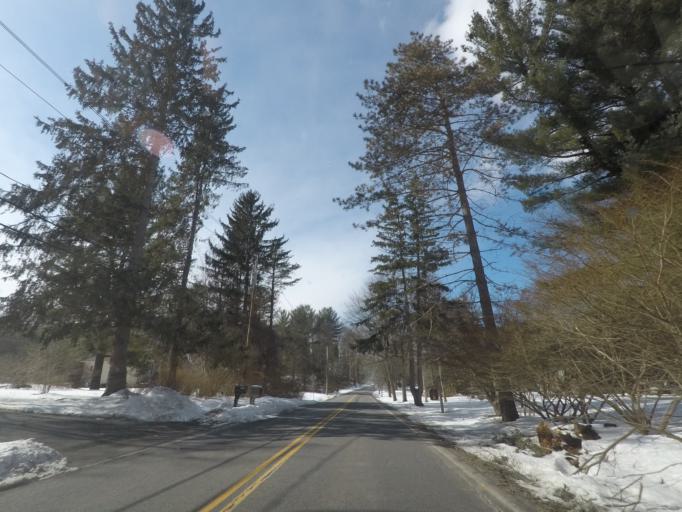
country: US
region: New York
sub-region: Albany County
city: Delmar
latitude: 42.6330
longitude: -73.8755
